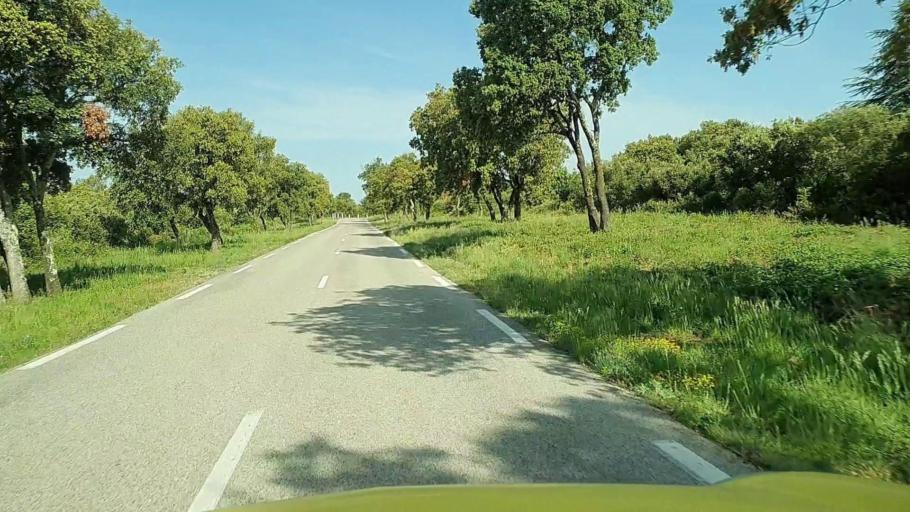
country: FR
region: Languedoc-Roussillon
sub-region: Departement du Gard
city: Montaren-et-Saint-Mediers
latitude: 44.1053
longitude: 4.3813
